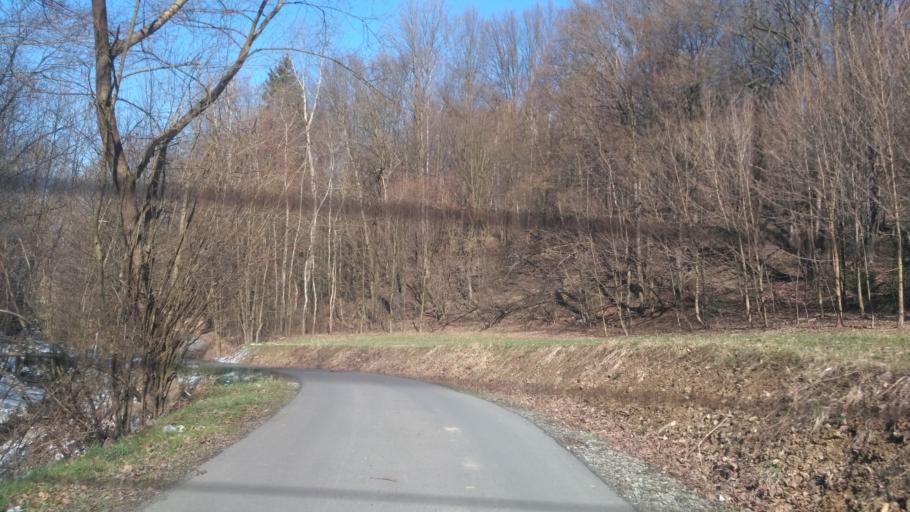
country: PL
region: Subcarpathian Voivodeship
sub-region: Powiat strzyzowski
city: Gwoznica Gorna
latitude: 49.8258
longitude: 22.0030
